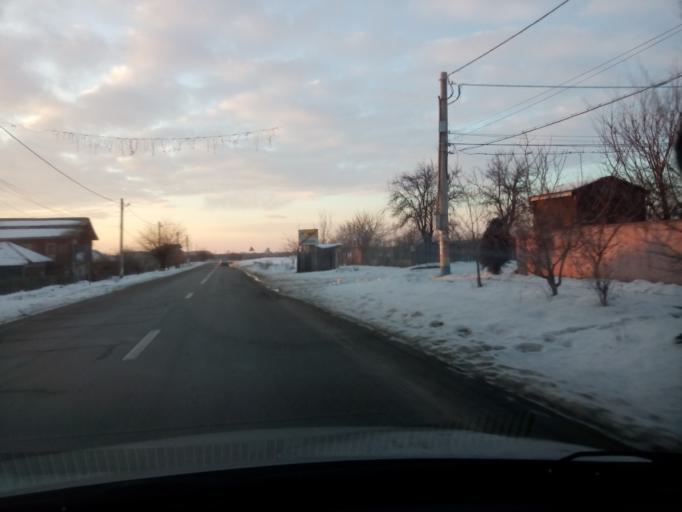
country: RO
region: Calarasi
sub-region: Comuna Soldanu
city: Soldanu
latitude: 44.2247
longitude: 26.5135
